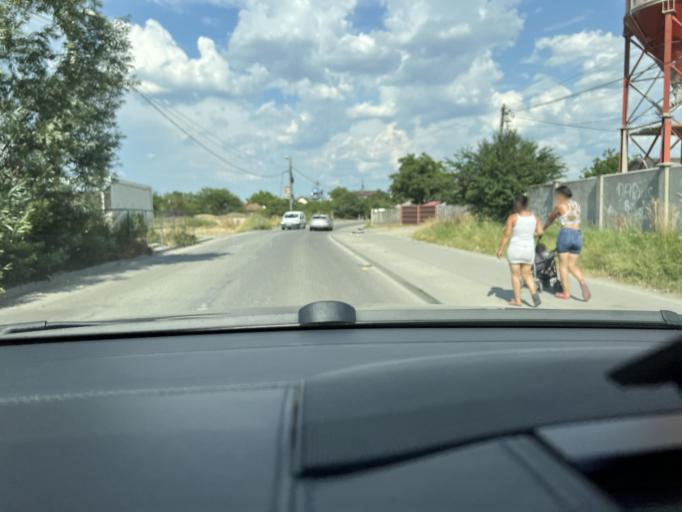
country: RO
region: Cluj
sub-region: Comuna Apahida
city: Sannicoara
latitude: 46.7791
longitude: 23.6910
